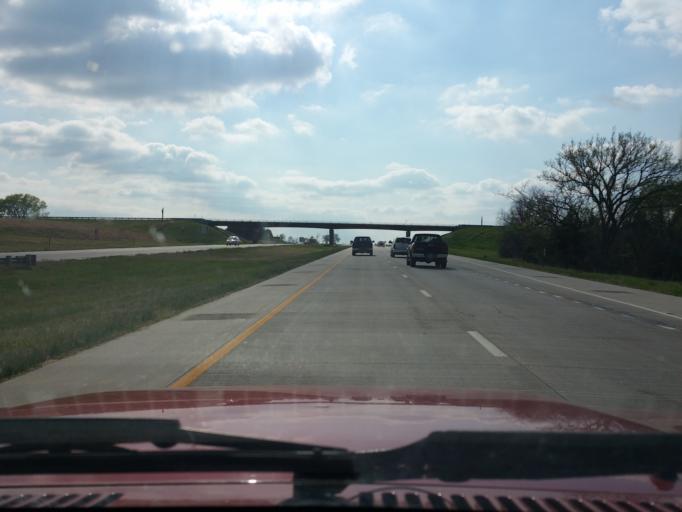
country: US
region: Kansas
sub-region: Wabaunsee County
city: Alma
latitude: 39.0655
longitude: -96.2395
